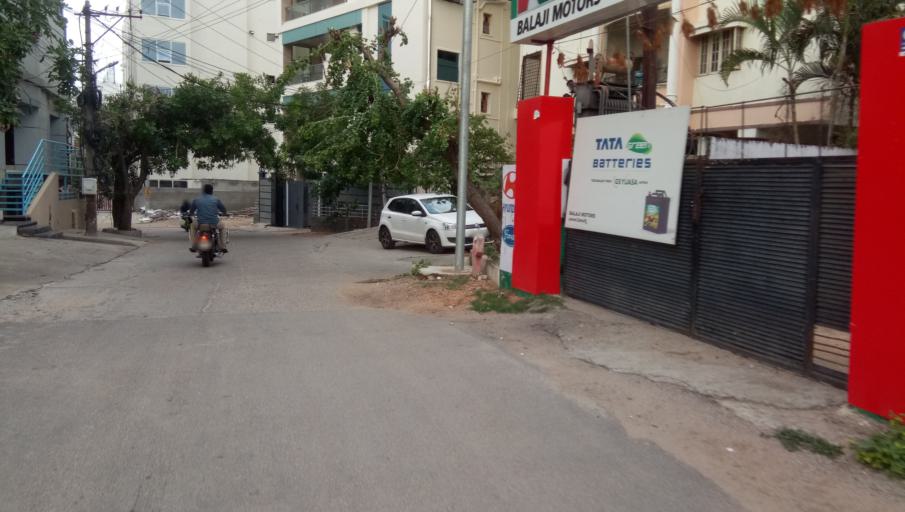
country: IN
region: Telangana
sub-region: Rangareddi
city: Gaddi Annaram
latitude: 17.3601
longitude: 78.5424
